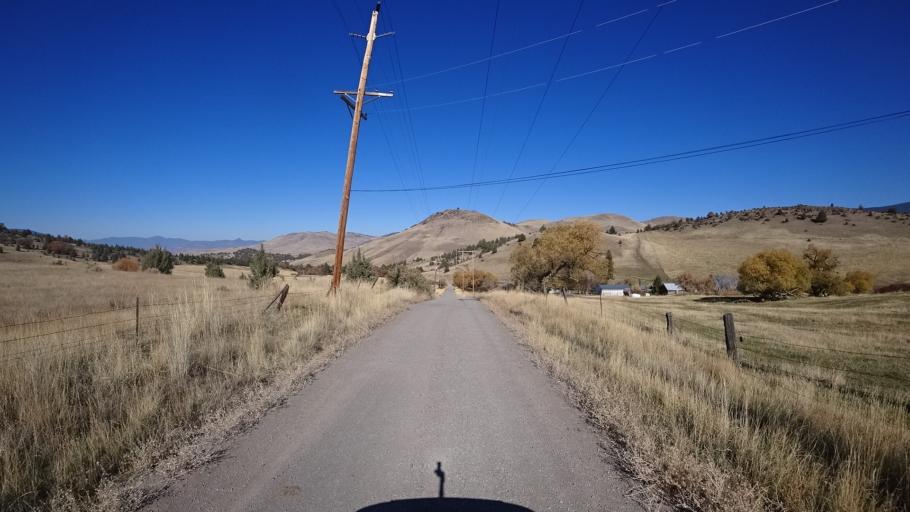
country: US
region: California
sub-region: Siskiyou County
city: Montague
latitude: 41.7845
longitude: -122.3590
